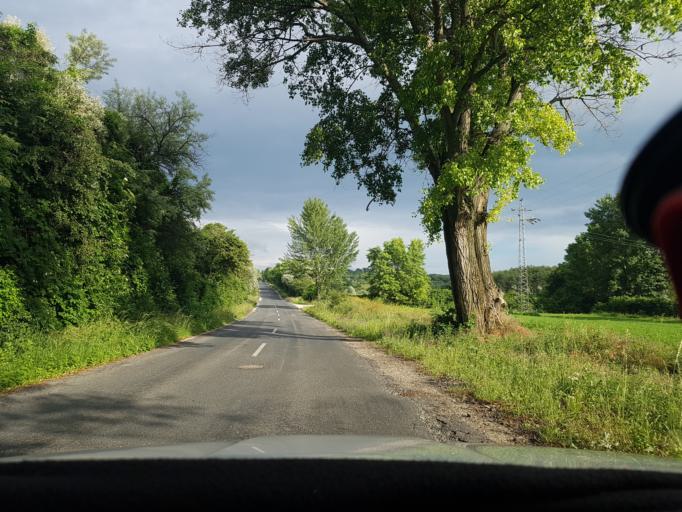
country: HU
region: Komarom-Esztergom
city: Labatlan
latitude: 47.7307
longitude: 18.5297
